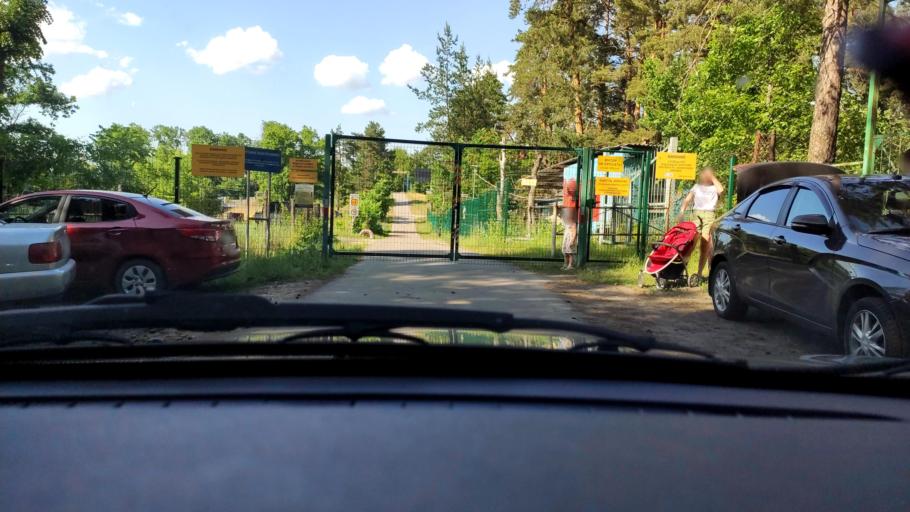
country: RU
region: Voronezj
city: Somovo
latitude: 51.8107
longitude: 39.3845
